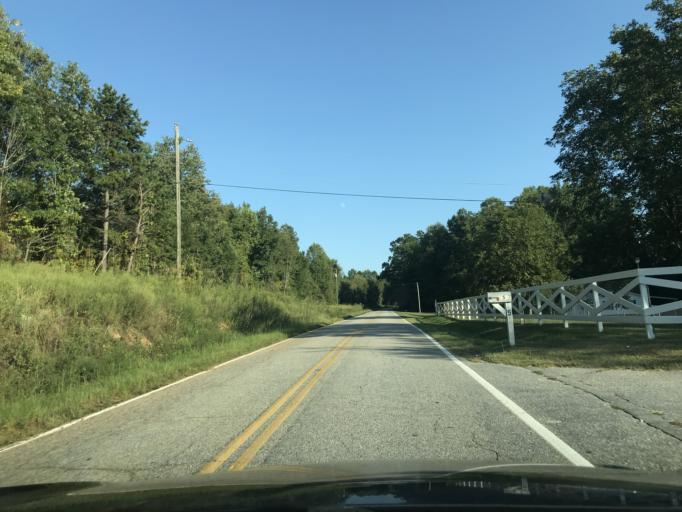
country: US
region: South Carolina
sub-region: Spartanburg County
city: Mayo
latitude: 35.1189
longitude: -81.7872
